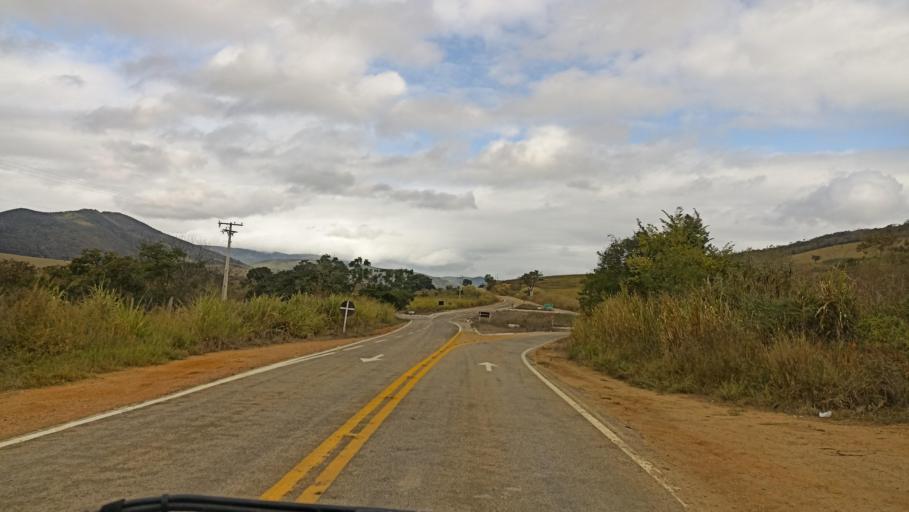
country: BR
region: Minas Gerais
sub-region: Joaima
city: Joaima
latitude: -16.6967
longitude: -40.9552
